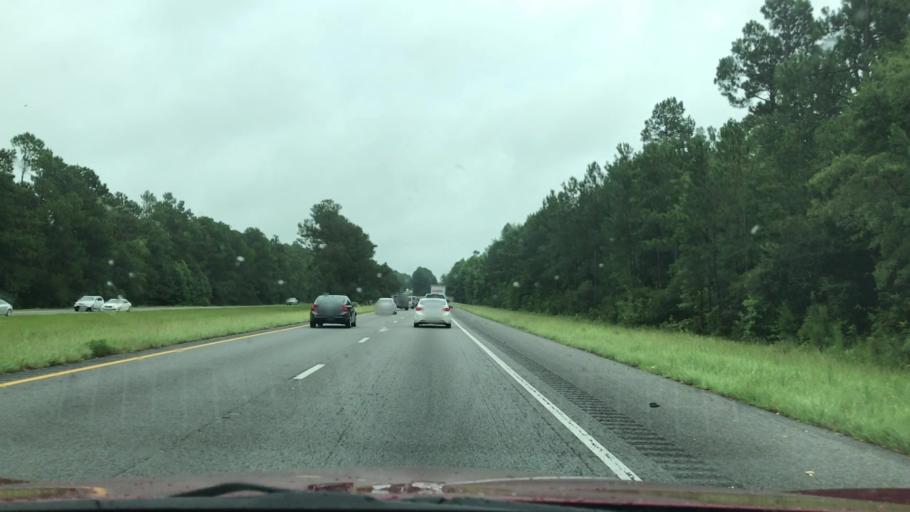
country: US
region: South Carolina
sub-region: Dorchester County
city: Ridgeville
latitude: 33.1694
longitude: -80.3640
